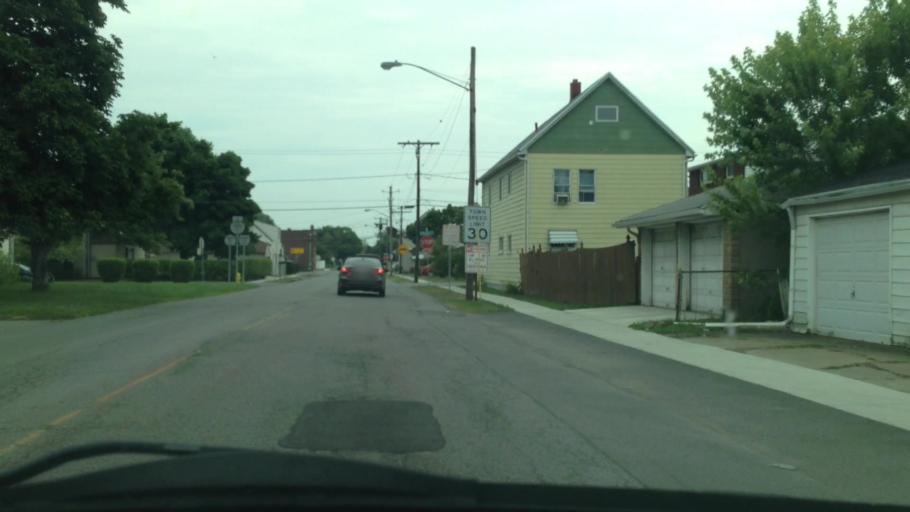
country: US
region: New York
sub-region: Erie County
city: Sloan
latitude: 42.8747
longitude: -78.7995
